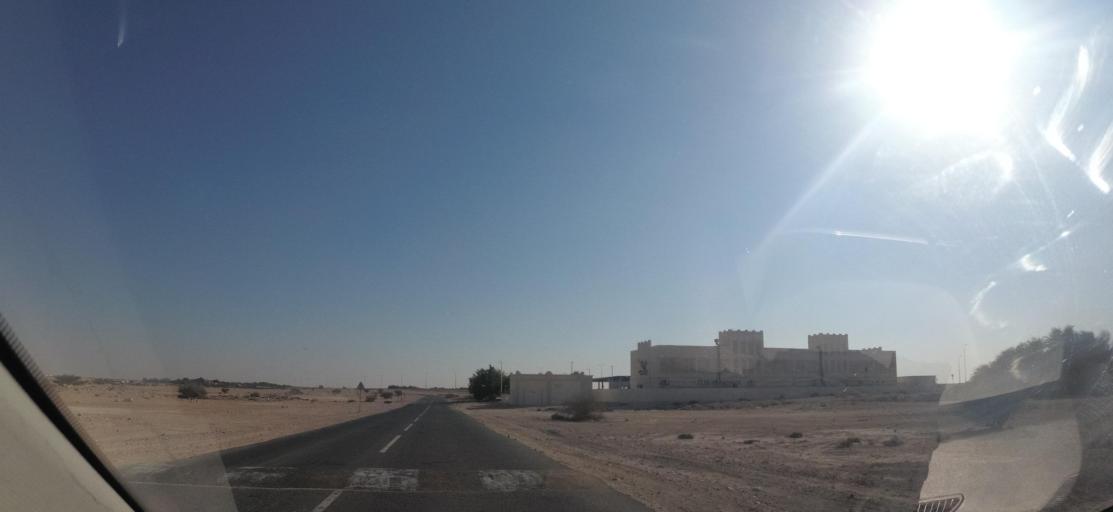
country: QA
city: Al Jumayliyah
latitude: 25.6181
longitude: 51.0855
